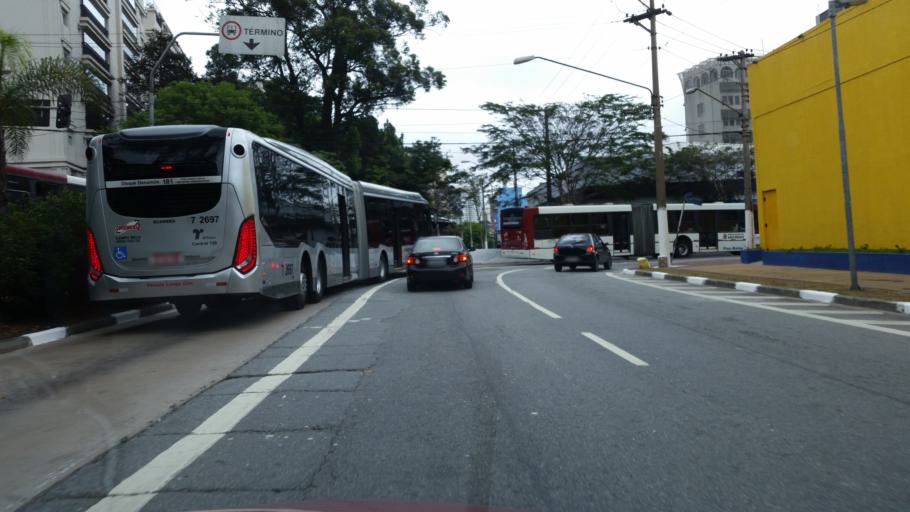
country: BR
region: Sao Paulo
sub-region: Diadema
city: Diadema
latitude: -23.6401
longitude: -46.6967
